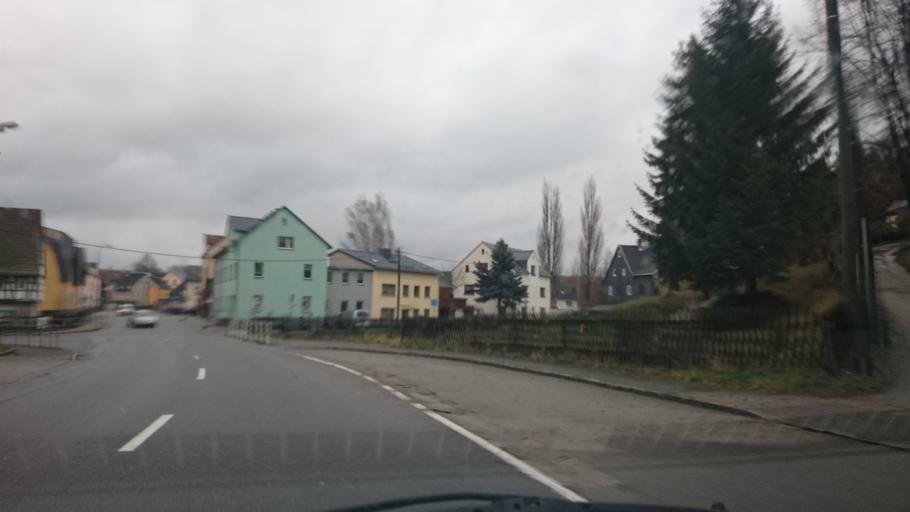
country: DE
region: Saxony
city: Sankt Egidien
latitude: 50.7839
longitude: 12.6194
